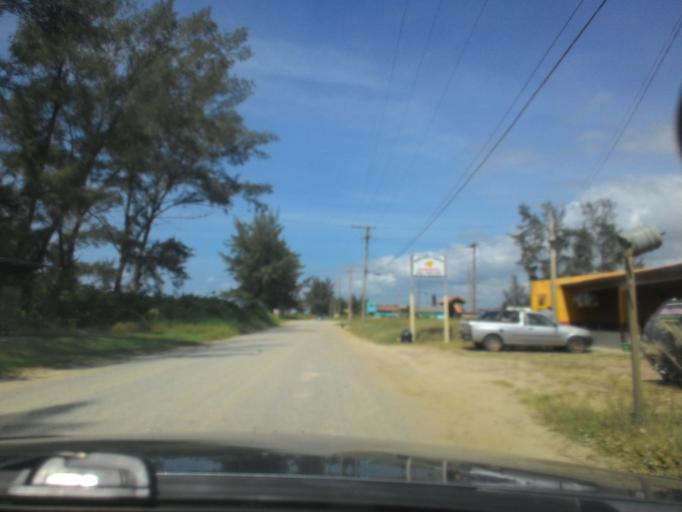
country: BR
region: Sao Paulo
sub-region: Iguape
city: Iguape
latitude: -24.8464
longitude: -47.6894
